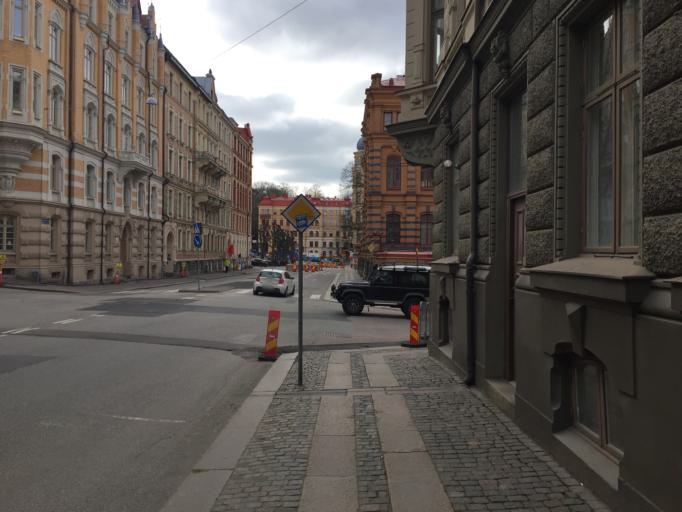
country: SE
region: Vaestra Goetaland
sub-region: Goteborg
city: Goeteborg
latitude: 57.6971
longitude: 11.9695
